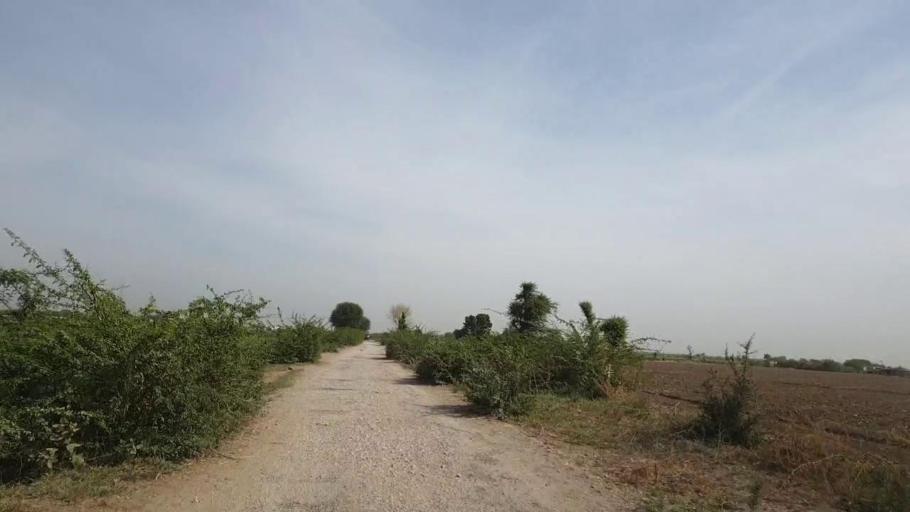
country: PK
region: Sindh
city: Kunri
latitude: 25.1731
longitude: 69.6257
